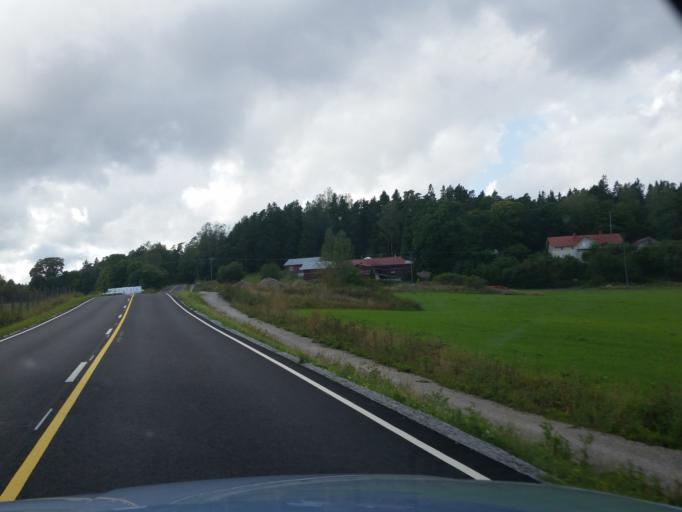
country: FI
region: Varsinais-Suomi
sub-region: Aboland-Turunmaa
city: Laensi-Turunmaa
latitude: 60.2446
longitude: 22.1974
